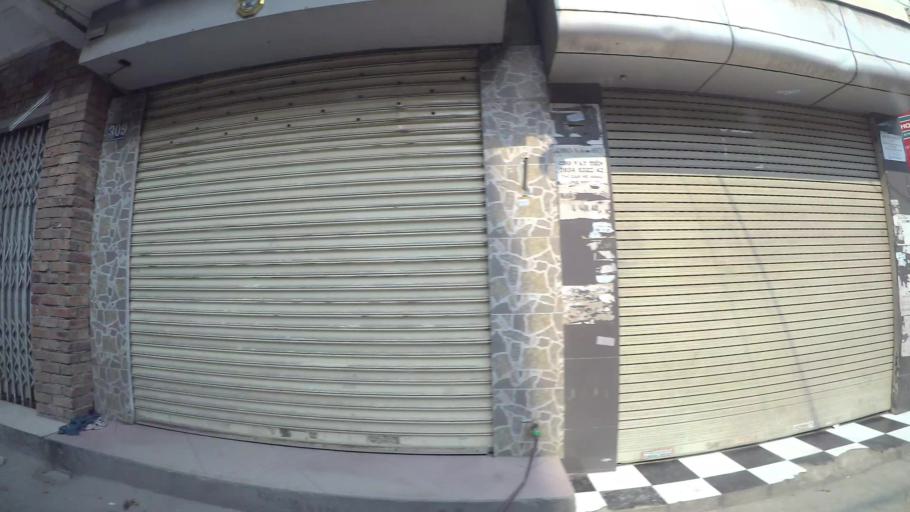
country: VN
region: Ha Noi
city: Thanh Xuan
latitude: 20.9845
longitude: 105.8197
